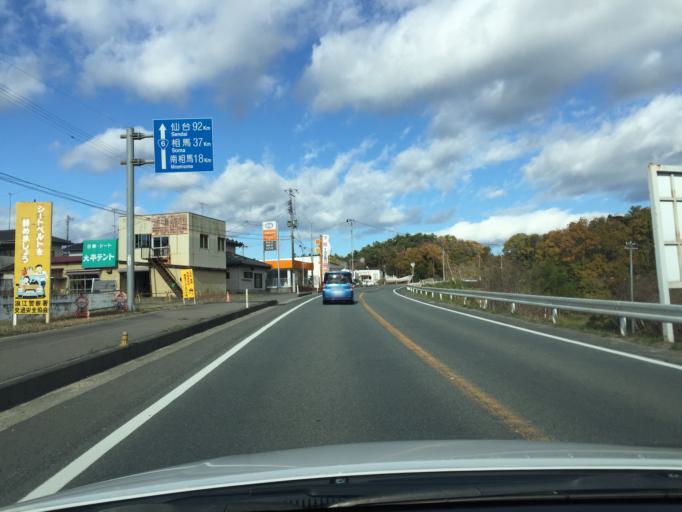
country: JP
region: Fukushima
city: Namie
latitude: 37.5032
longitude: 140.9980
